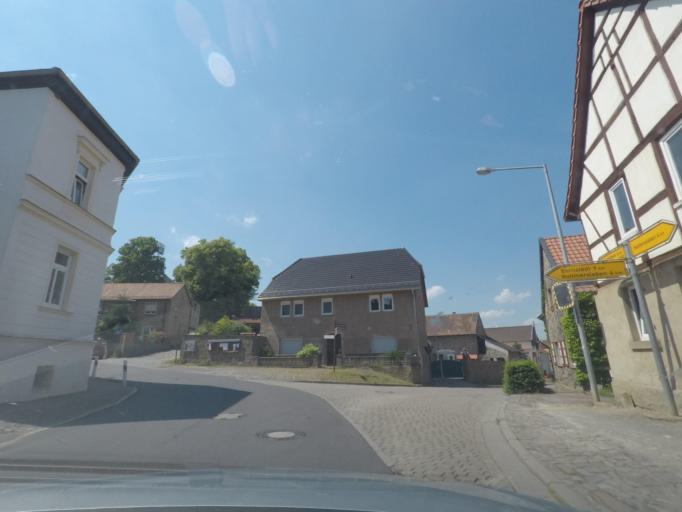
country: DE
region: Saxony-Anhalt
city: Haldensleben I
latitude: 52.2474
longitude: 11.3998
